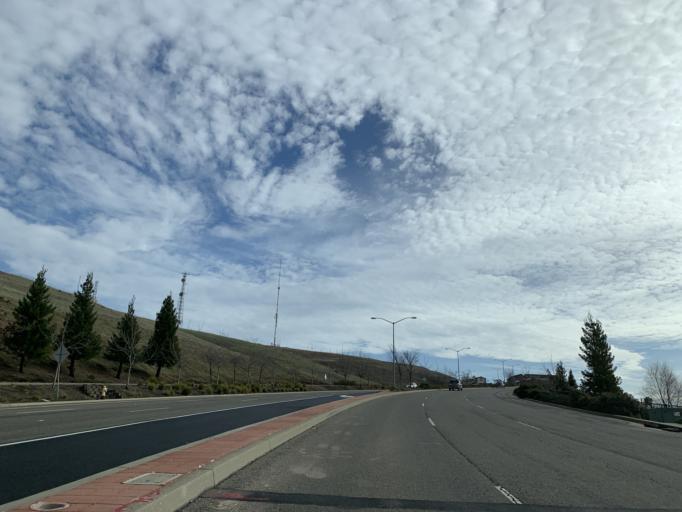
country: US
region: California
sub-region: El Dorado County
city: El Dorado Hills
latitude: 38.6479
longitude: -121.1038
